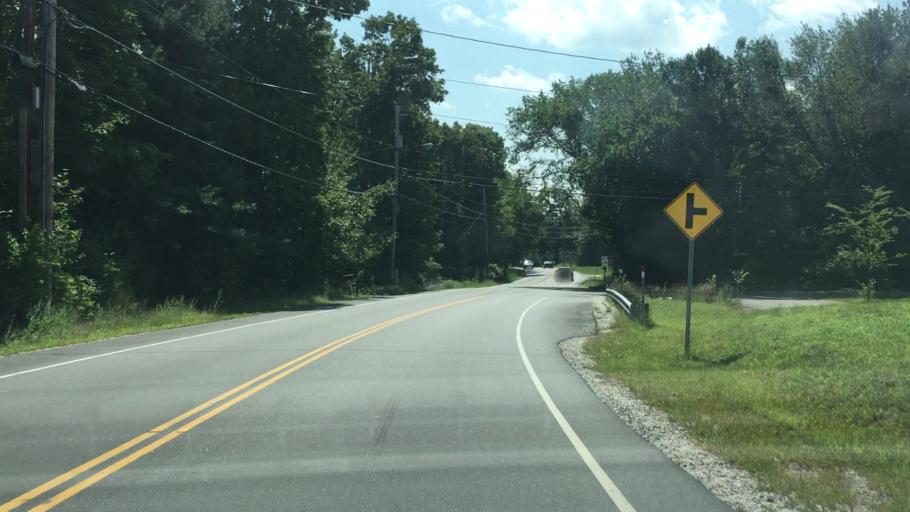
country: US
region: New Hampshire
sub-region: Rockingham County
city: Windham
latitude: 42.7916
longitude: -71.3555
